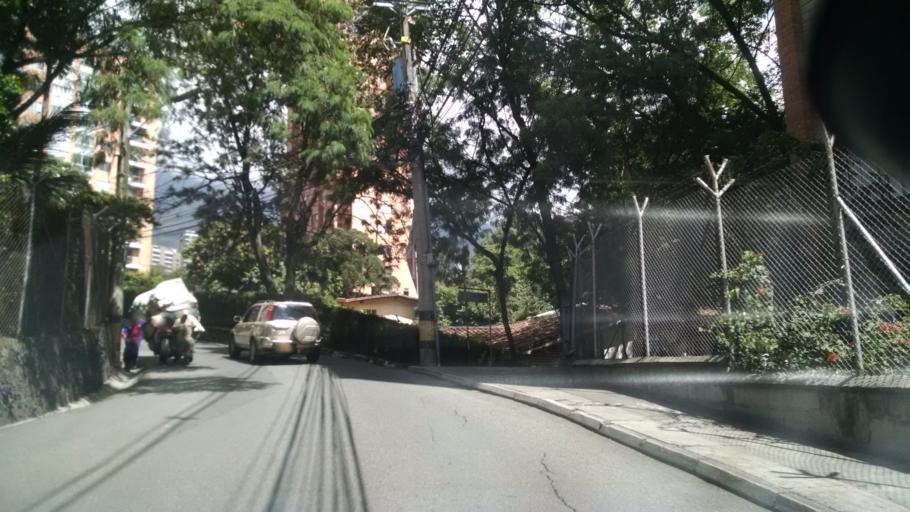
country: CO
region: Antioquia
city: Medellin
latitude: 6.2119
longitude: -75.5674
